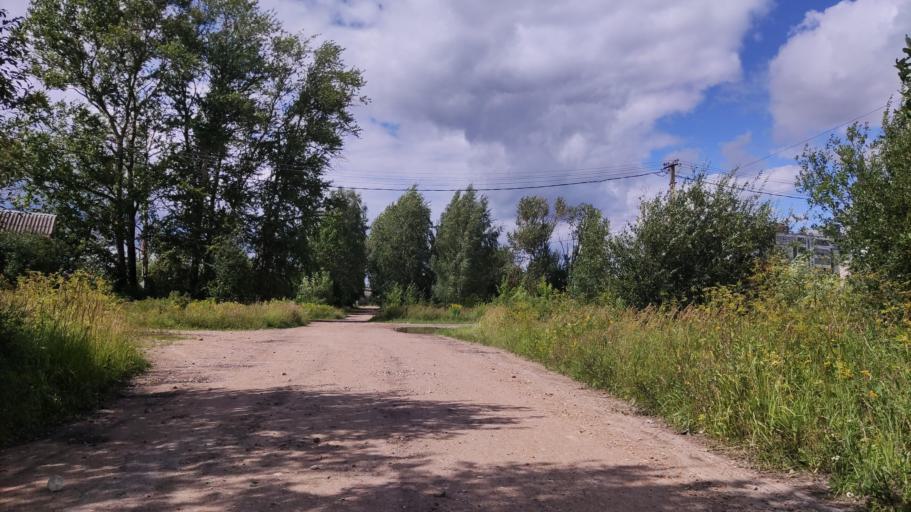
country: RU
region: Tverskaya
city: Rzhev
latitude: 56.2401
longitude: 34.3050
